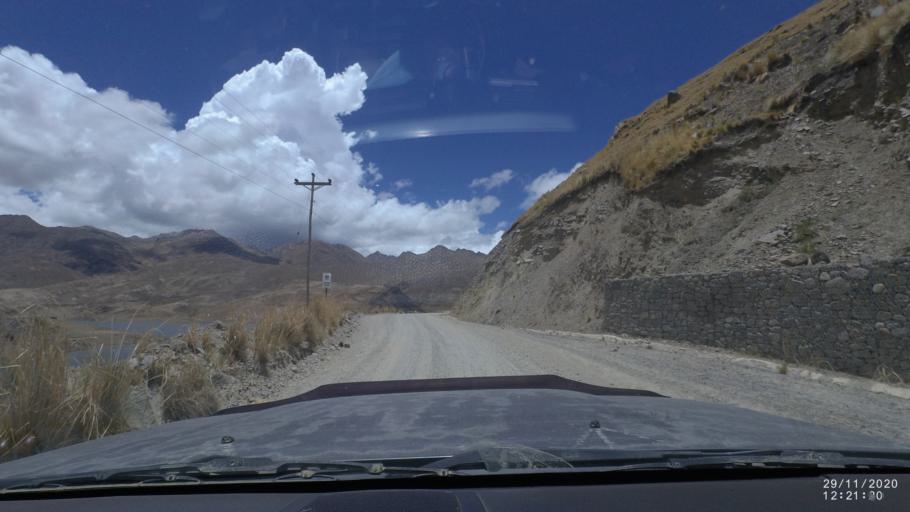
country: BO
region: Cochabamba
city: Cochabamba
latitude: -17.0986
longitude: -66.3216
